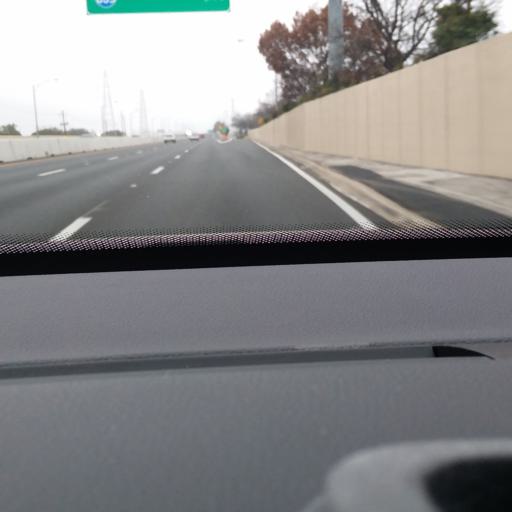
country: US
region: Texas
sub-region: Dallas County
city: University Park
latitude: 32.8970
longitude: -96.8089
